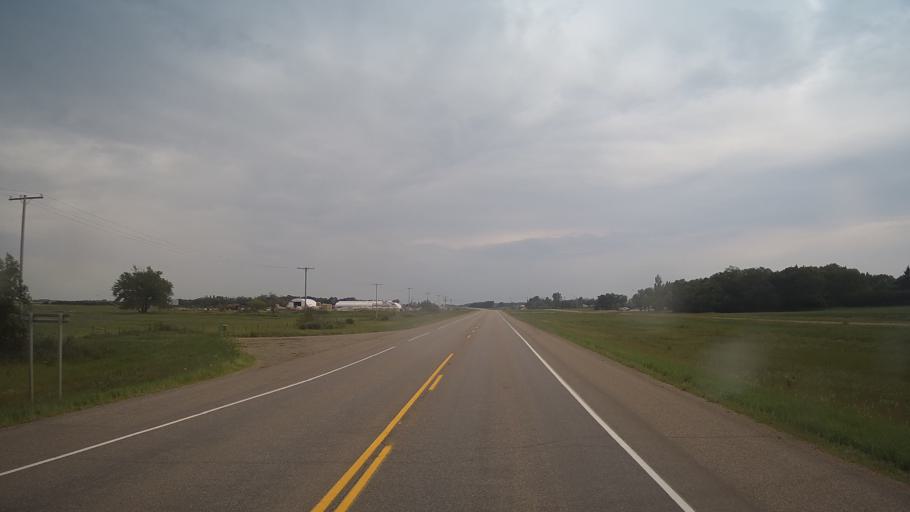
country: CA
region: Saskatchewan
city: Langham
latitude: 52.1289
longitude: -107.2201
